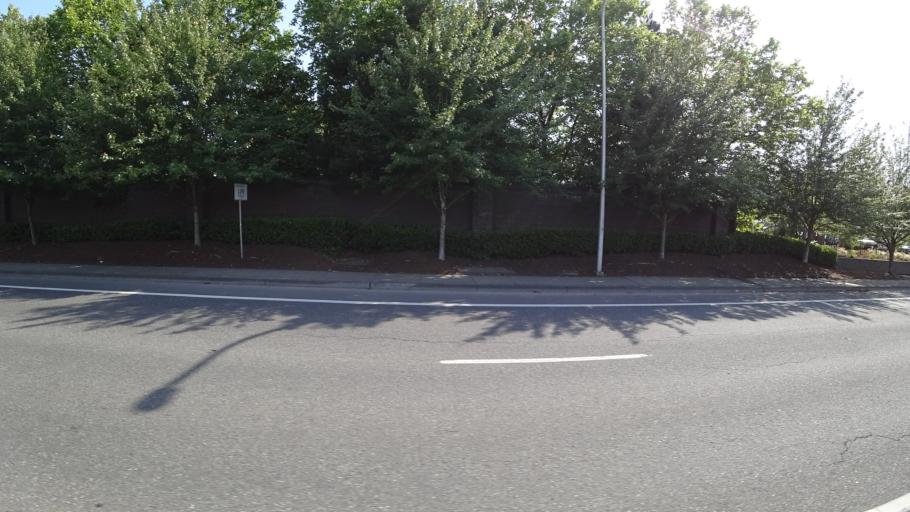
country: US
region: Oregon
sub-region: Clackamas County
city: Sunnyside
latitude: 45.4330
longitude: -122.5477
